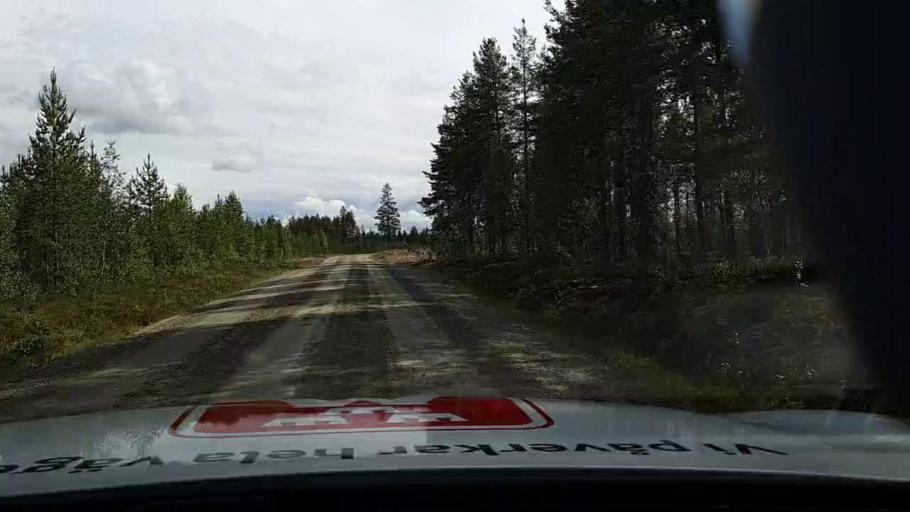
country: SE
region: Jaemtland
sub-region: Are Kommun
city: Jarpen
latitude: 62.5039
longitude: 13.5003
